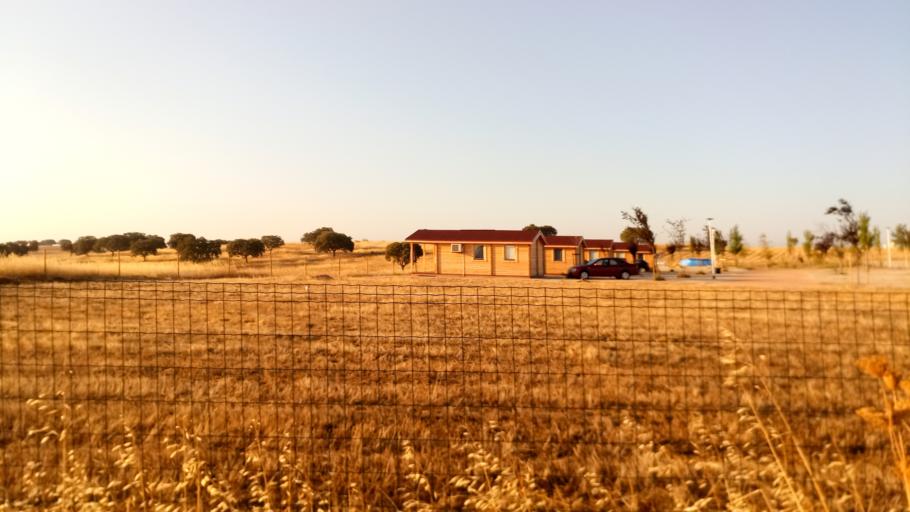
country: PT
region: Evora
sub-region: Reguengos de Monsaraz
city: Reguengos de Monsaraz
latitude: 38.3589
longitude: -7.4643
